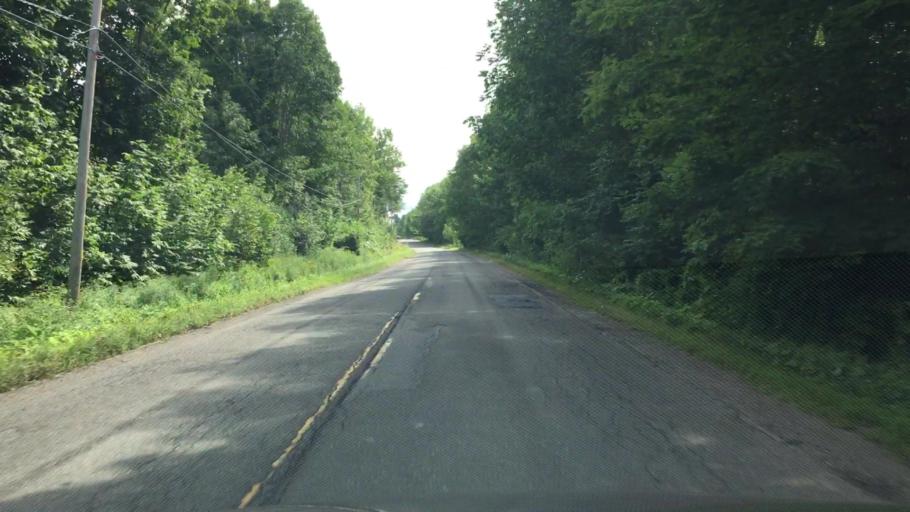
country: US
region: Maine
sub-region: Penobscot County
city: Hampden
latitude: 44.7270
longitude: -68.8634
